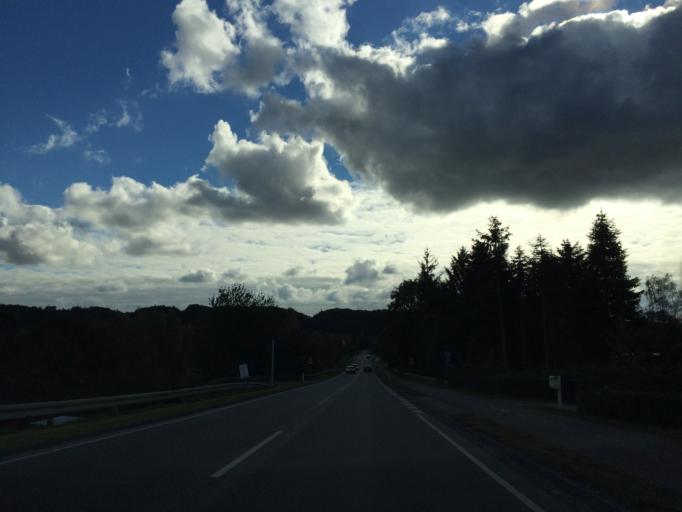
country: DK
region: Central Jutland
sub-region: Skanderborg Kommune
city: Ry
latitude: 56.1062
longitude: 9.7846
